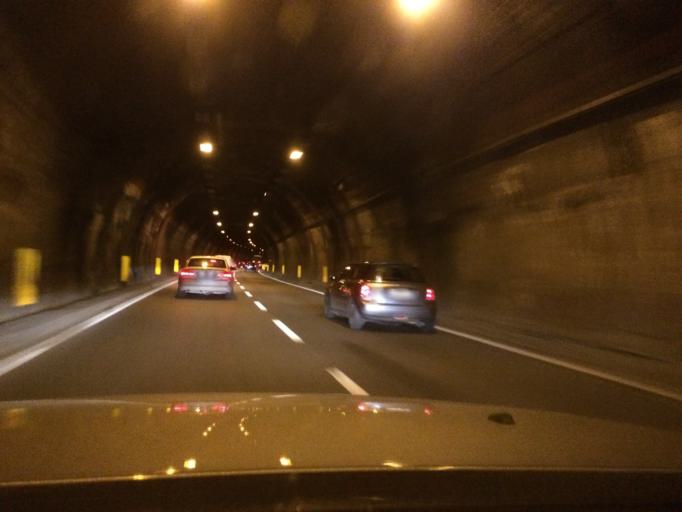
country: IT
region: Umbria
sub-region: Provincia di Perugia
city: Perugia
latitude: 43.0943
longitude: 12.3831
